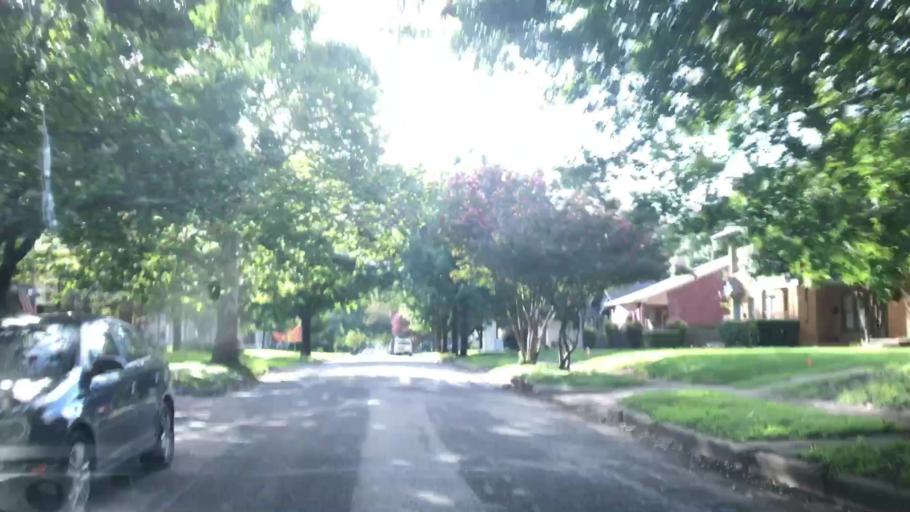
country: US
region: Texas
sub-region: Dallas County
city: Highland Park
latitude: 32.8213
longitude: -96.7777
